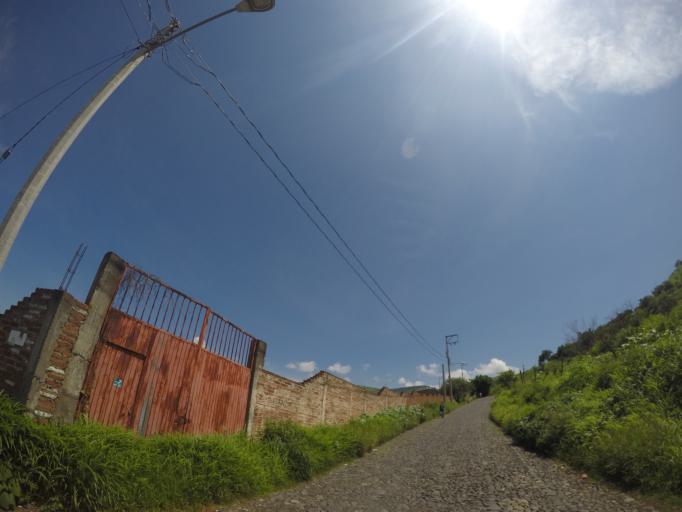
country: MX
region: Nayarit
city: Ixtlan del Rio
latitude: 21.0357
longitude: -104.3608
